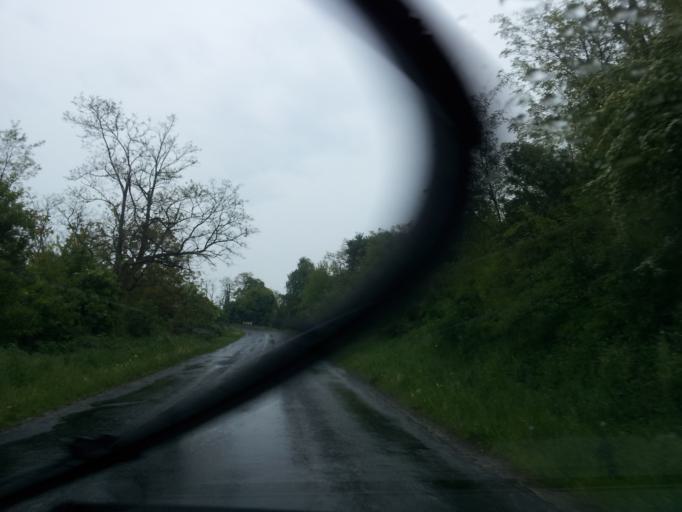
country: HU
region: Tolna
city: Szekszard
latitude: 46.2882
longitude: 18.6711
